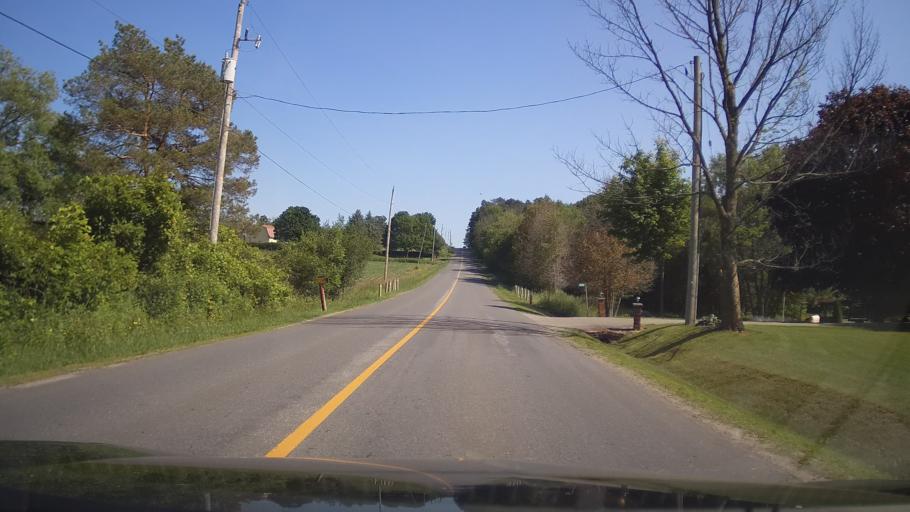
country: CA
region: Ontario
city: Oshawa
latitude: 43.9532
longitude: -78.7268
